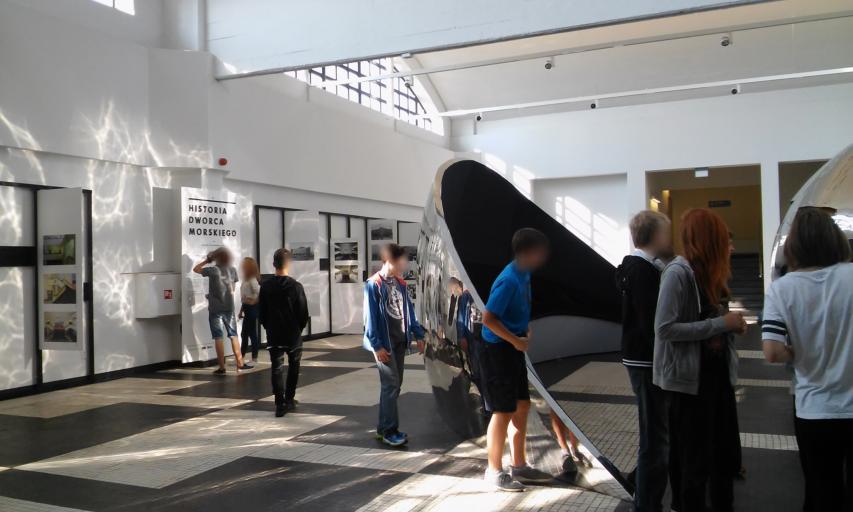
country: PL
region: Pomeranian Voivodeship
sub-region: Gdynia
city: Gdynia
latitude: 54.5331
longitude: 18.5485
